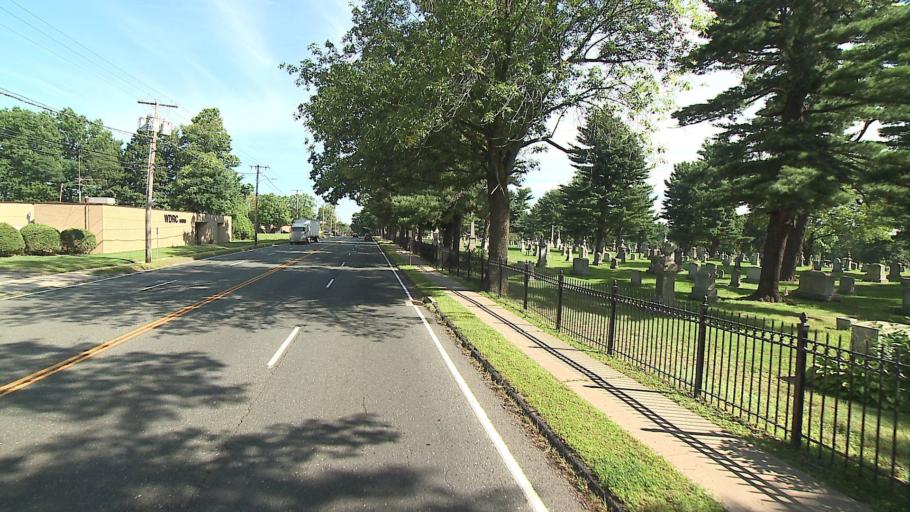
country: US
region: Connecticut
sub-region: Hartford County
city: Blue Hills
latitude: 41.8129
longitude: -72.6947
